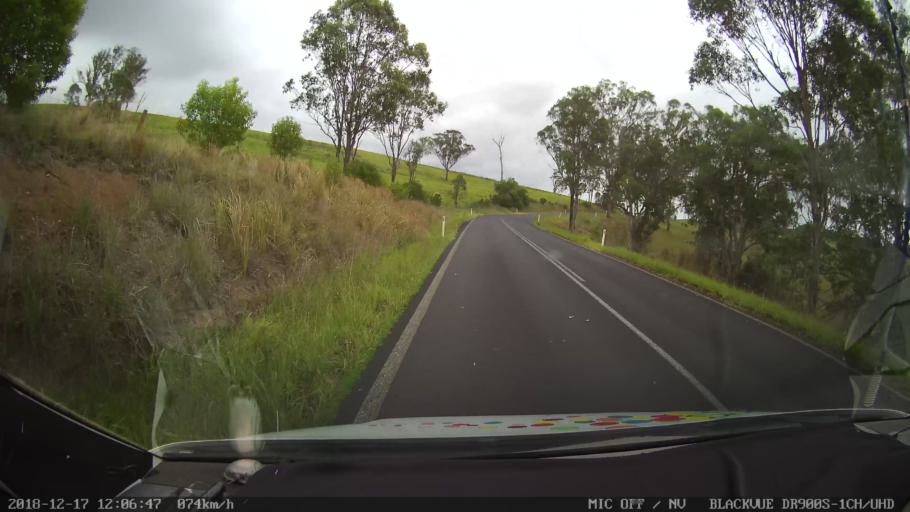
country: AU
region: New South Wales
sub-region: Kyogle
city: Kyogle
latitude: -28.4784
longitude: 152.5659
